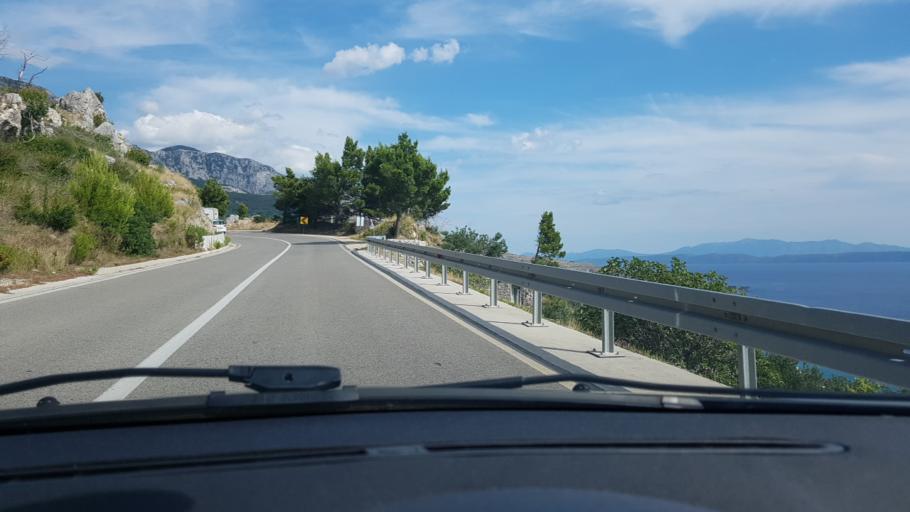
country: HR
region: Splitsko-Dalmatinska
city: Tucepi
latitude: 43.2779
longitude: 17.0512
